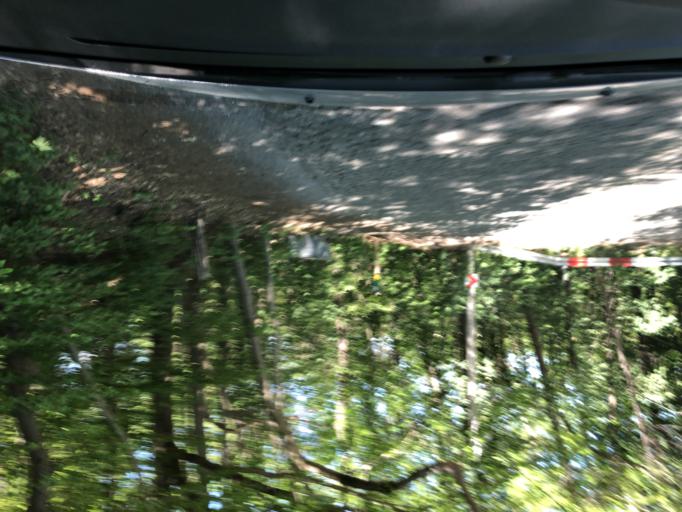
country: DE
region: Saxony
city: Radebeul
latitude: 51.0593
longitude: 13.6461
